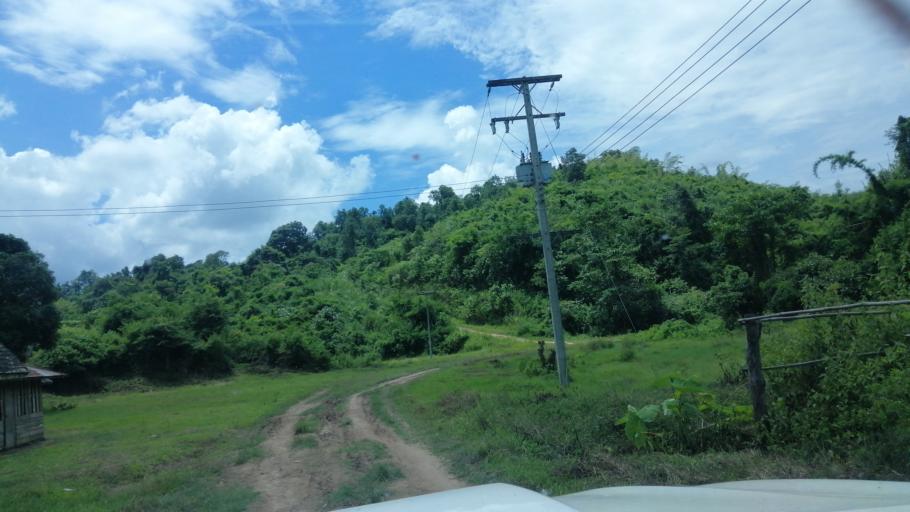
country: TH
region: Nan
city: Chaloem Phra Kiat
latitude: 19.7246
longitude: 101.4360
